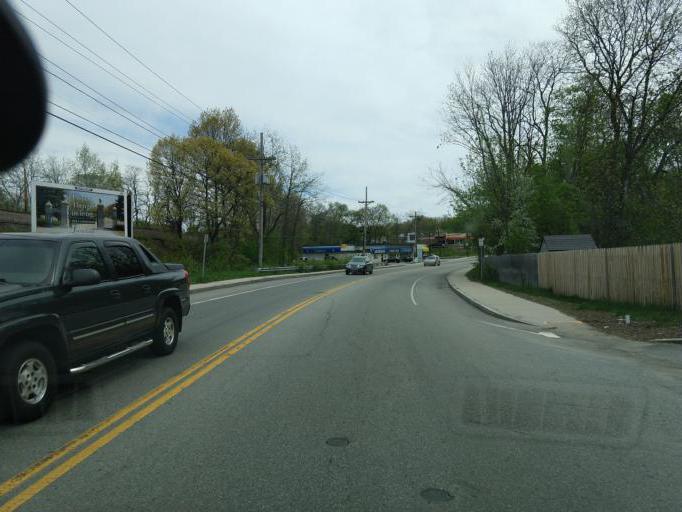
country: US
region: Massachusetts
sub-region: Essex County
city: Haverhill
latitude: 42.7578
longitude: -71.1012
